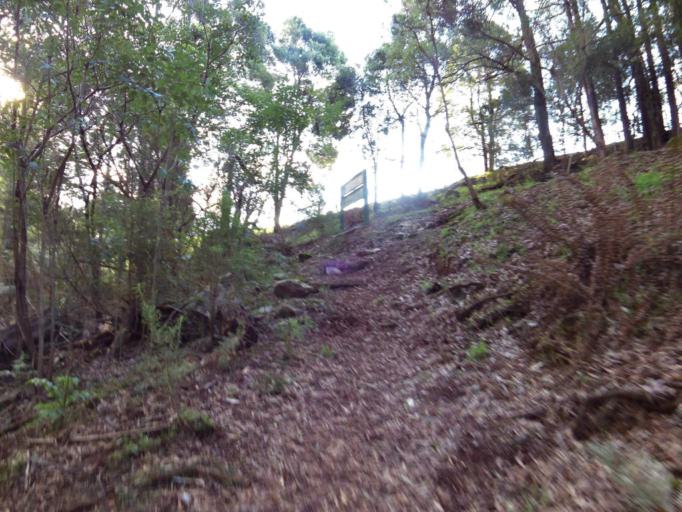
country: AU
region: Victoria
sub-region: Baw Baw
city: Warragul
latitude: -37.9273
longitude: 145.9427
